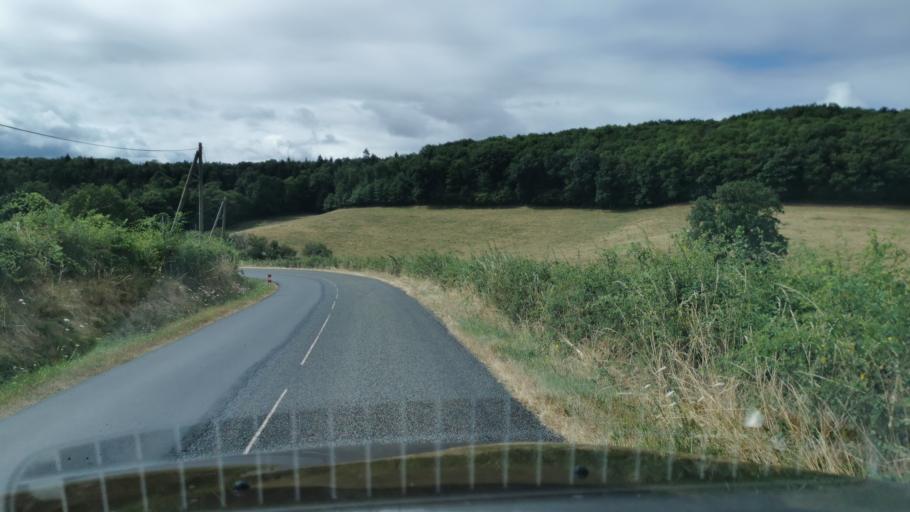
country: FR
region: Bourgogne
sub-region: Departement de Saone-et-Loire
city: Montcenis
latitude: 46.7965
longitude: 4.3656
